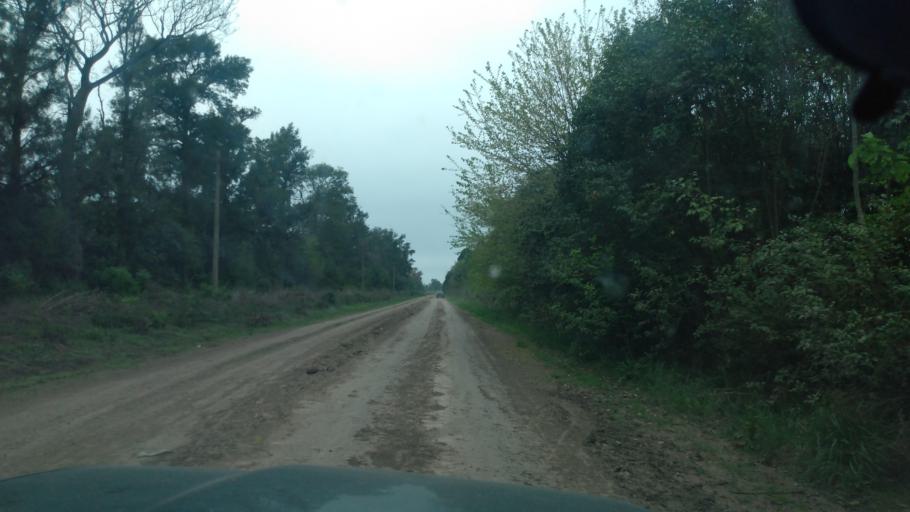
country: AR
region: Buenos Aires
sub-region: Partido de Lujan
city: Lujan
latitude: -34.5411
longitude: -59.2048
